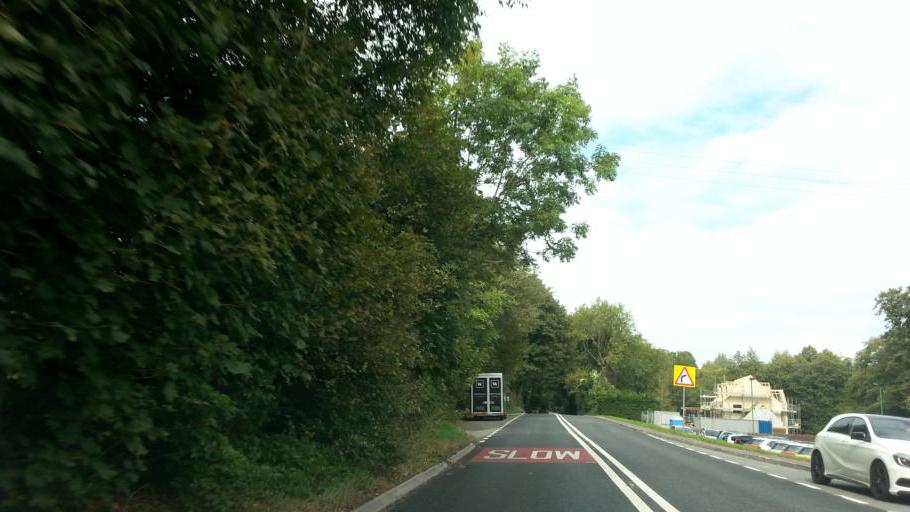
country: GB
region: England
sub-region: Gloucestershire
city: Stroud
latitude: 51.7609
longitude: -2.2221
